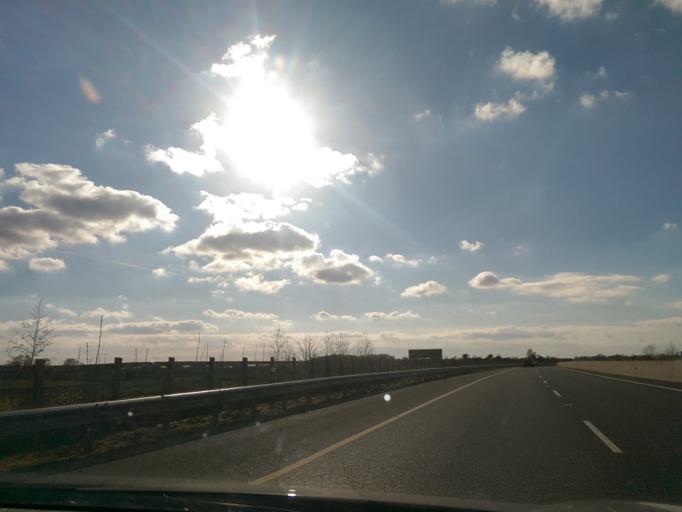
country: IE
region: Connaught
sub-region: County Galway
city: Loughrea
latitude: 53.2657
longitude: -8.6305
